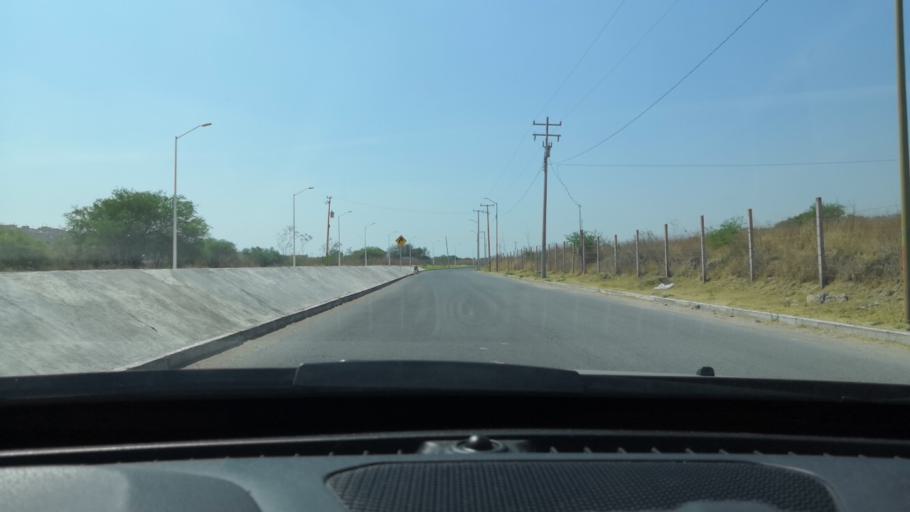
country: MX
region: Guanajuato
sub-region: Purisima del Rincon
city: Potrerillos (Guanajal)
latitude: 21.0564
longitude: -101.8680
